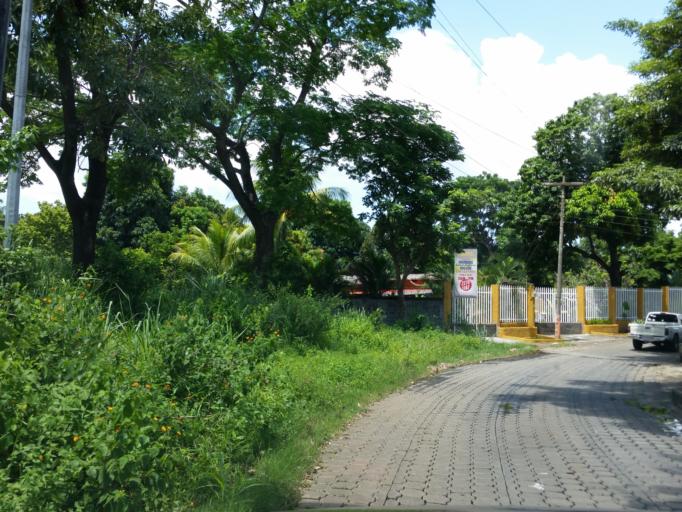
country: NI
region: Managua
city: Managua
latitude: 12.0991
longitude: -86.2409
